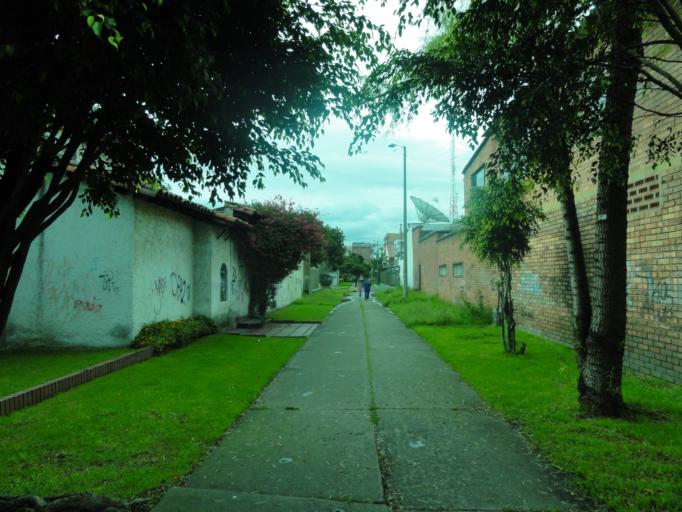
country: CO
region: Bogota D.C.
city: Bogota
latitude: 4.6455
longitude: -74.0824
